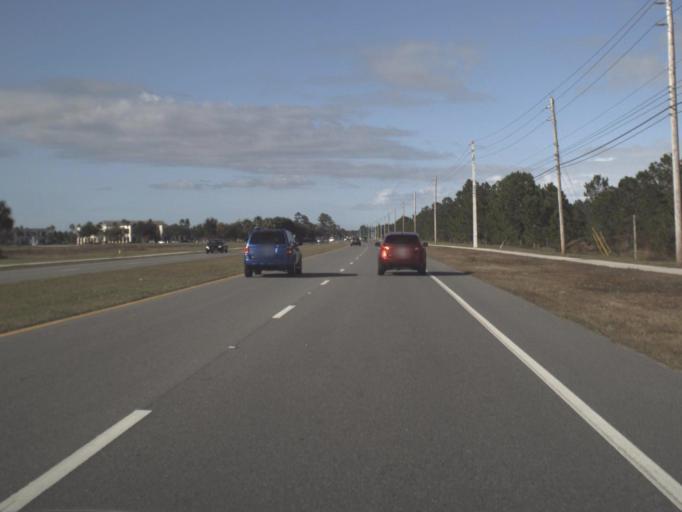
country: US
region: Florida
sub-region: Volusia County
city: Holly Hill
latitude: 29.2174
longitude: -81.0915
